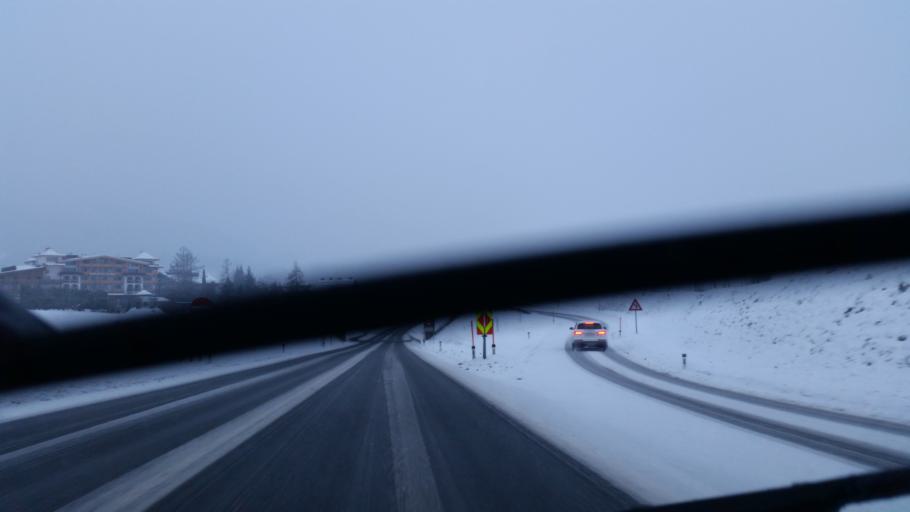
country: AT
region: Tyrol
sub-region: Politischer Bezirk Kufstein
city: Ellmau
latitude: 47.5155
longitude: 12.3111
